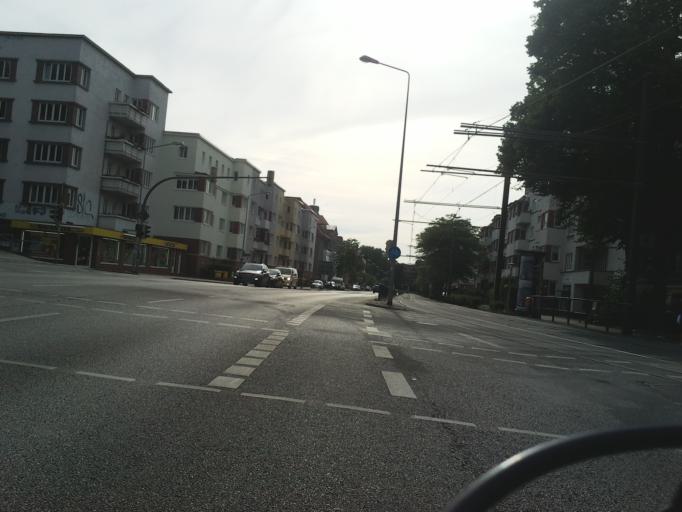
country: DE
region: Mecklenburg-Vorpommern
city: Rostock
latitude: 54.0848
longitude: 12.1159
